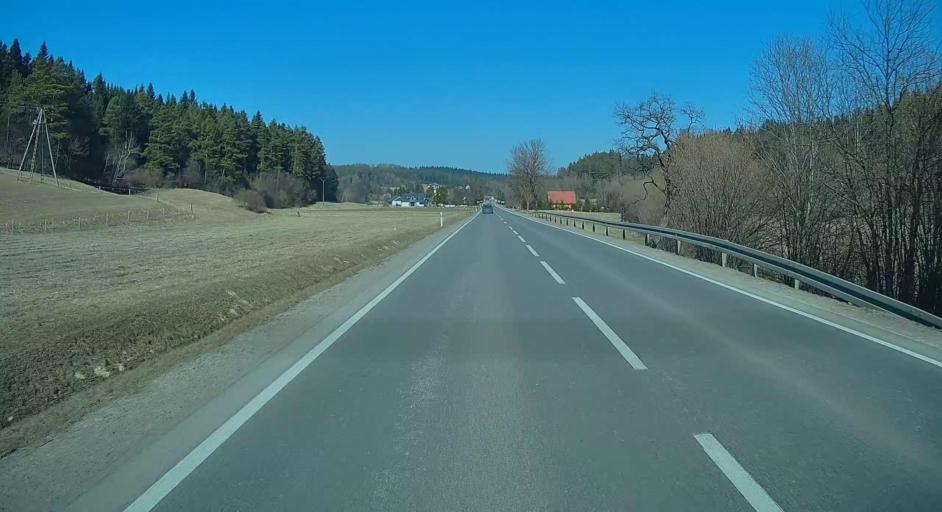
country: PL
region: Subcarpathian Voivodeship
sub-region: Powiat przemyski
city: Bircza
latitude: 49.6816
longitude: 22.4375
